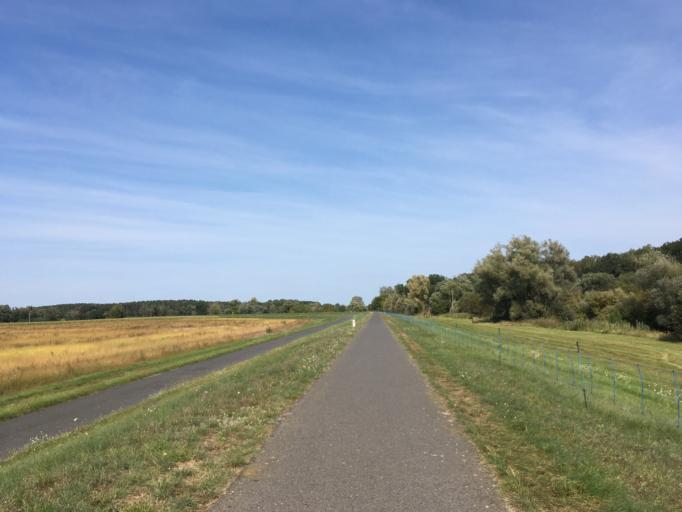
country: PL
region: Lubusz
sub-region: Powiat krosnienski
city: Gubin
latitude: 52.0476
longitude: 14.7454
